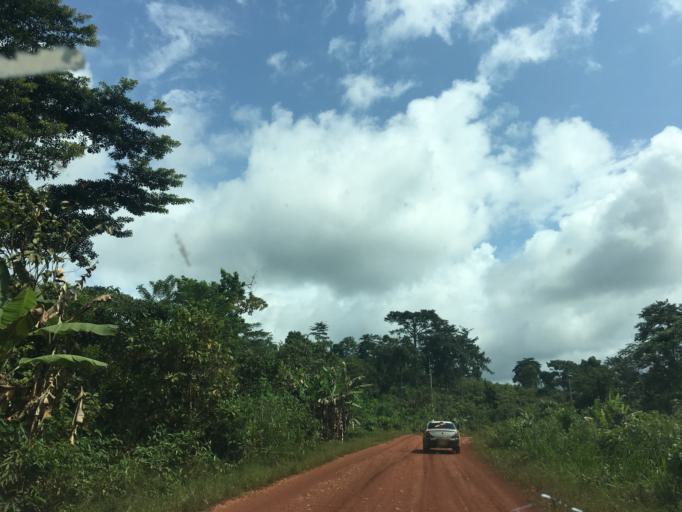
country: GH
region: Western
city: Wassa-Akropong
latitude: 5.7848
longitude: -2.3900
